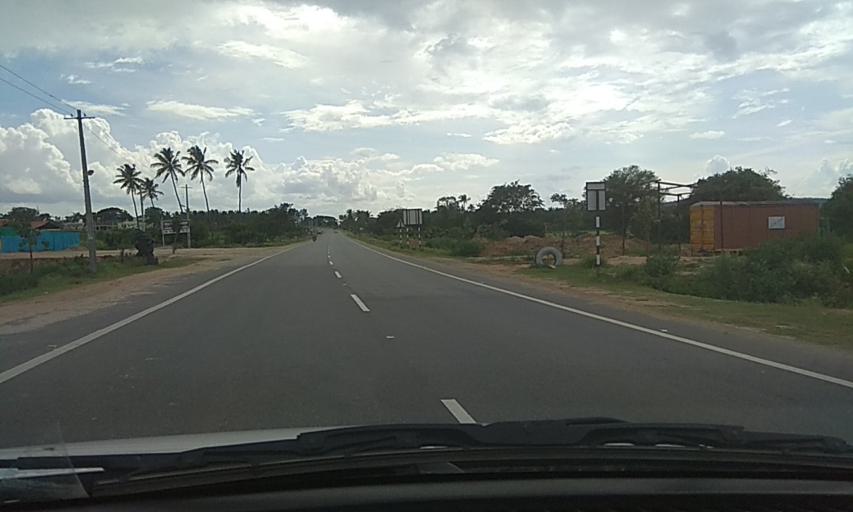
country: IN
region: Karnataka
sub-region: Tumkur
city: Kunigal
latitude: 12.8385
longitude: 77.0334
